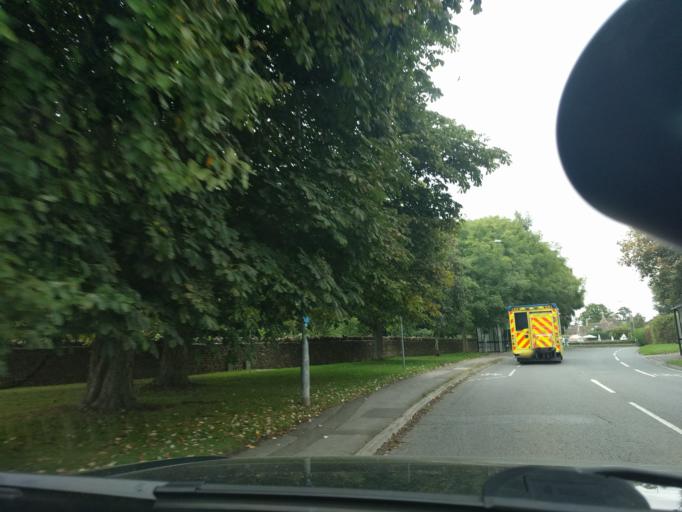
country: GB
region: England
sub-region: Wiltshire
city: Corsham
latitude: 51.4328
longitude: -2.1980
